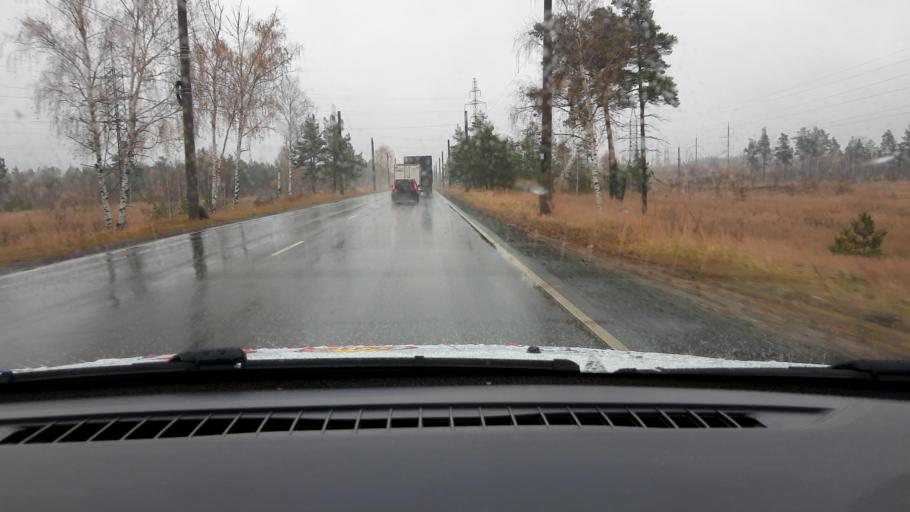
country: RU
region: Nizjnij Novgorod
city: Babino
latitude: 56.2829
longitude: 43.5761
